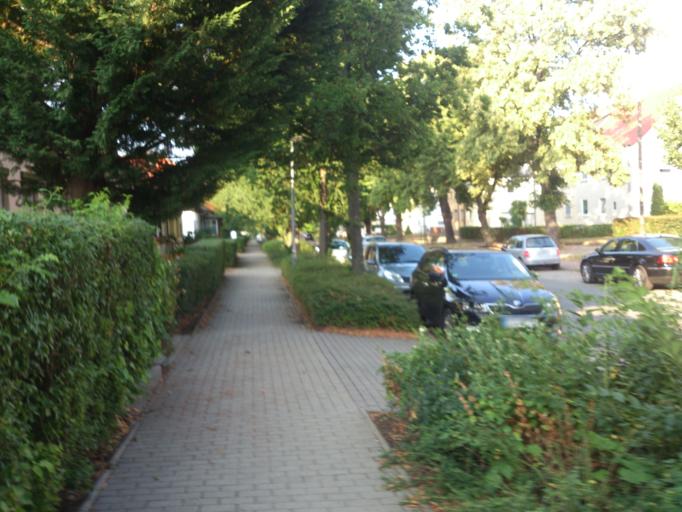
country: DE
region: Saxony-Anhalt
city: Quedlinburg
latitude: 51.7778
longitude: 11.1494
